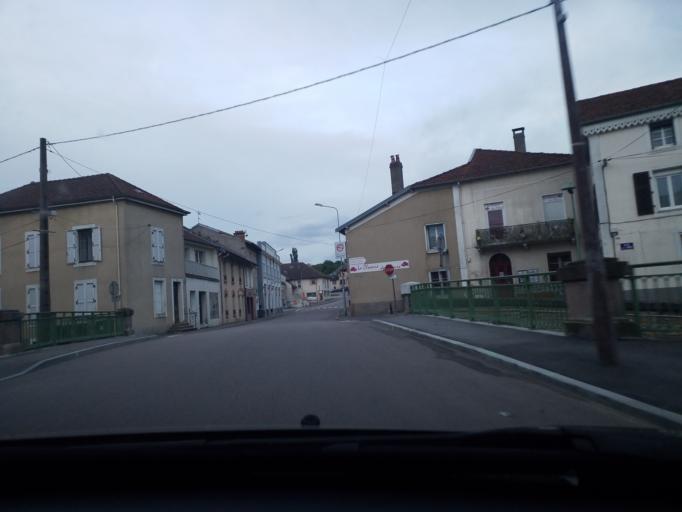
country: FR
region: Lorraine
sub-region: Departement des Vosges
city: Vittel
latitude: 48.1993
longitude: 5.9508
